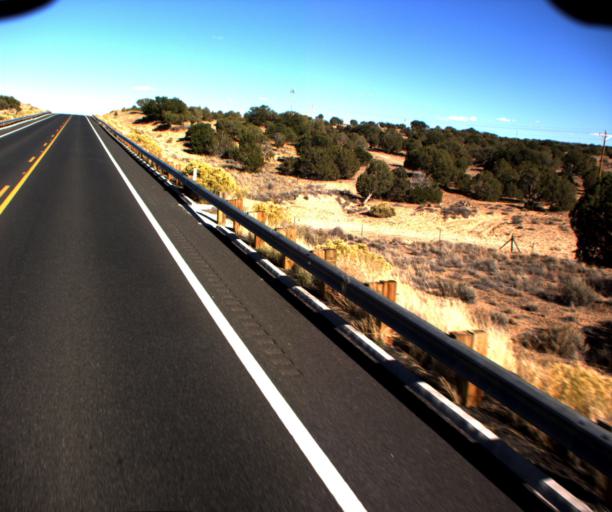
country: US
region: Arizona
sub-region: Coconino County
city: Kaibito
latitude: 36.4450
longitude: -110.7304
